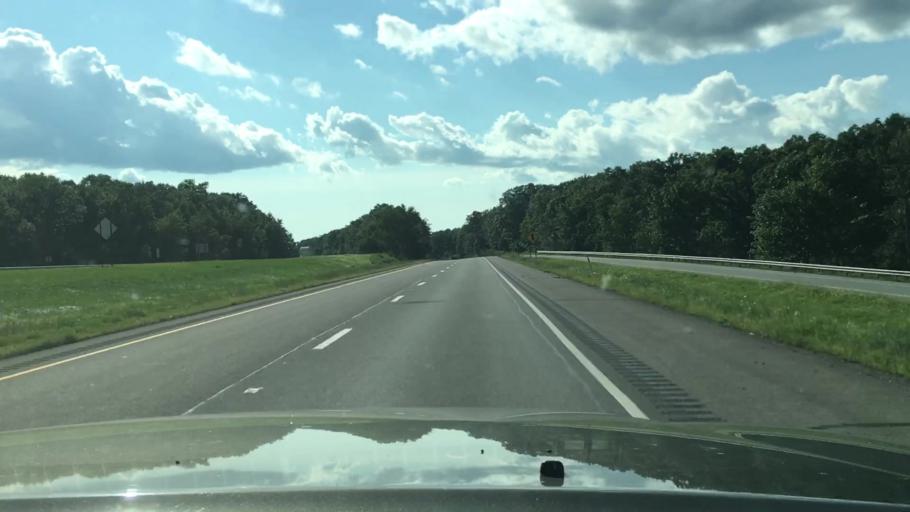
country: US
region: Pennsylvania
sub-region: Wayne County
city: Hawley
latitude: 41.3610
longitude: -75.2043
